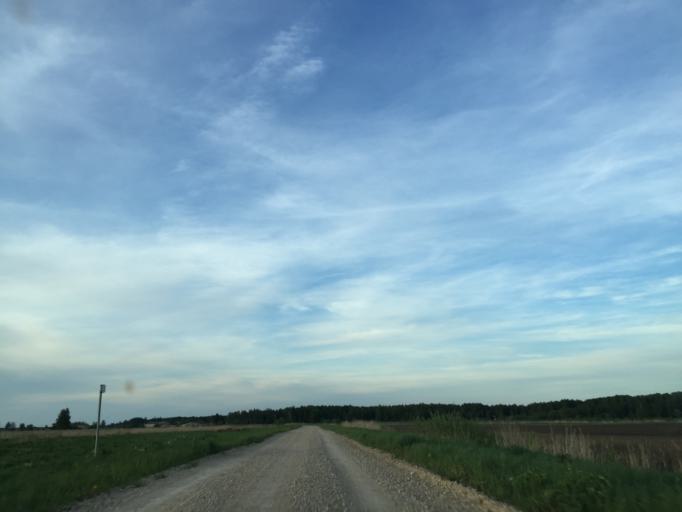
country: LV
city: Tireli
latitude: 56.7787
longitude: 23.5536
